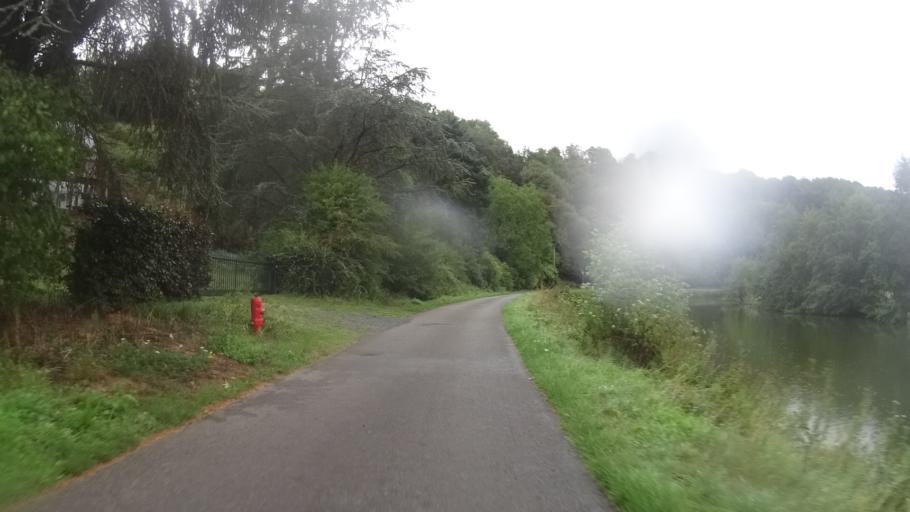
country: BE
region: Wallonia
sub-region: Province du Hainaut
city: Lobbes
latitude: 50.3471
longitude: 4.2740
